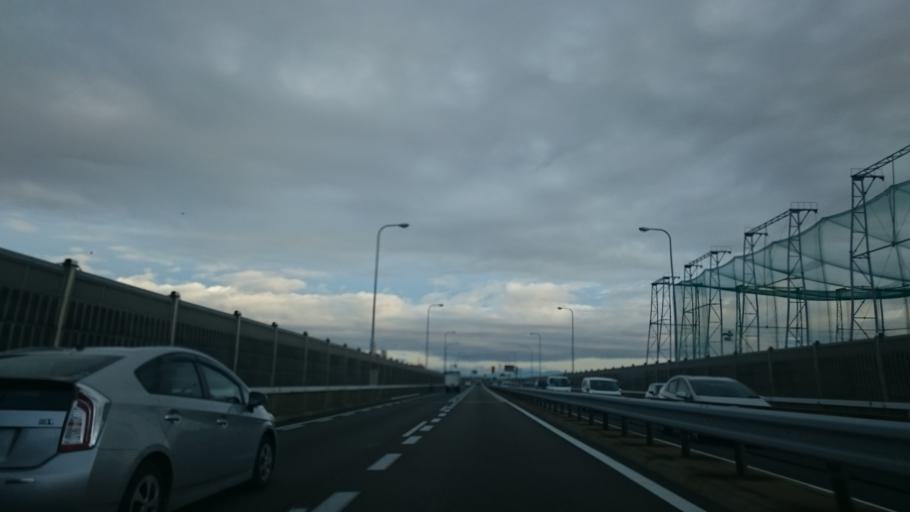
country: JP
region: Aichi
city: Kanie
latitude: 35.1913
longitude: 136.8165
